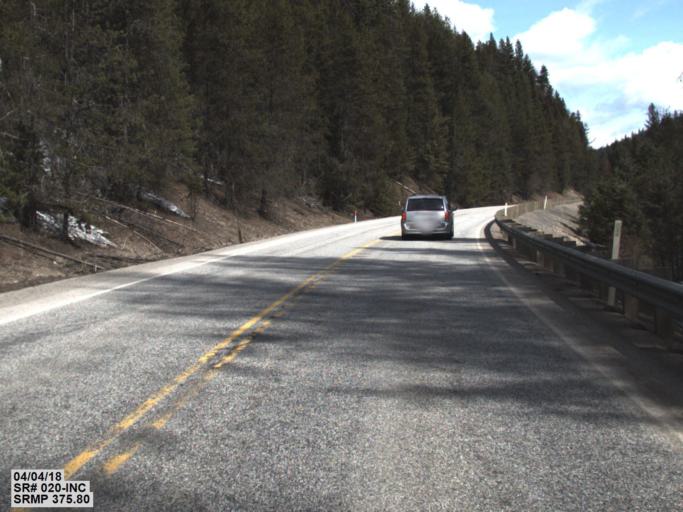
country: US
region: Washington
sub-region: Stevens County
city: Chewelah
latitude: 48.5667
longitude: -117.5557
